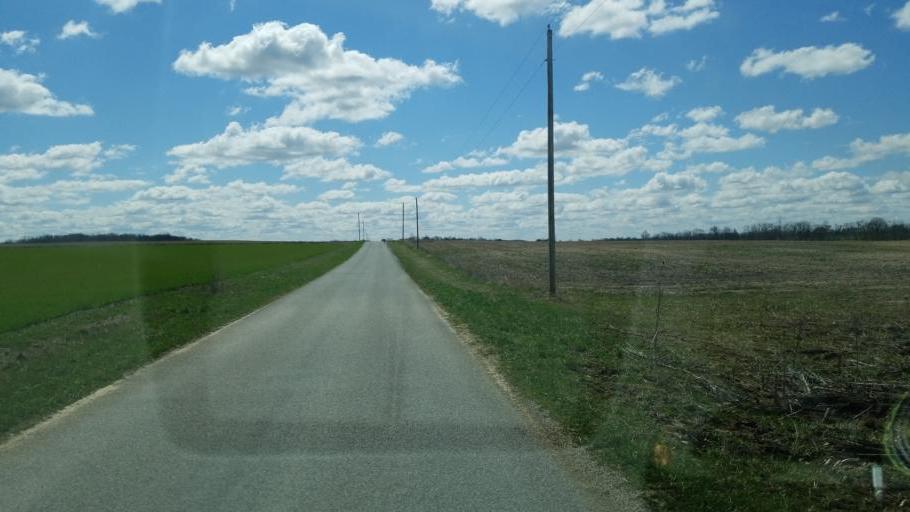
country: US
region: Ohio
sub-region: Hancock County
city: Findlay
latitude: 41.0592
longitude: -83.5149
